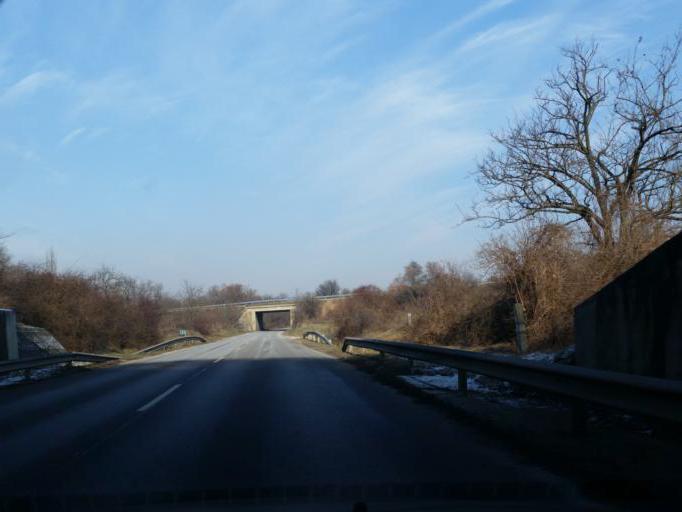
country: HU
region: Pest
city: Biatorbagy
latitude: 47.4882
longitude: 18.8255
